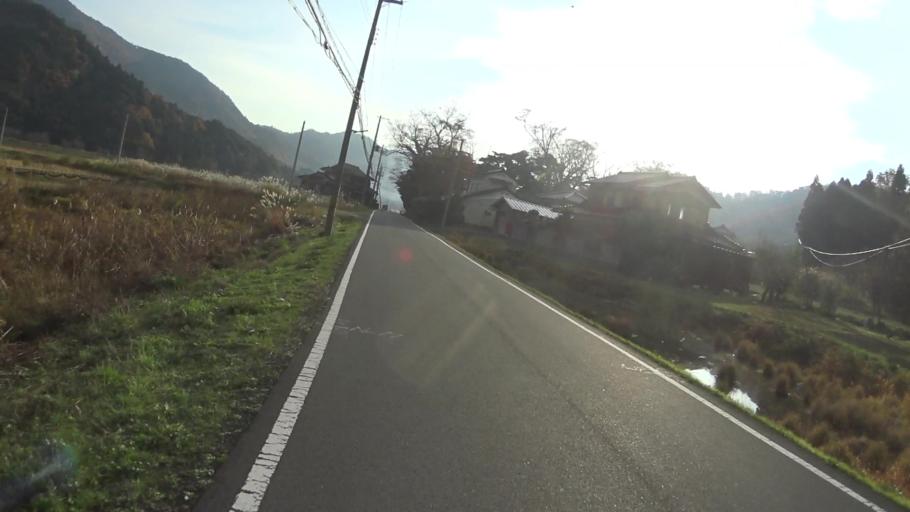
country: JP
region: Kyoto
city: Maizuru
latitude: 35.5229
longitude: 135.4067
